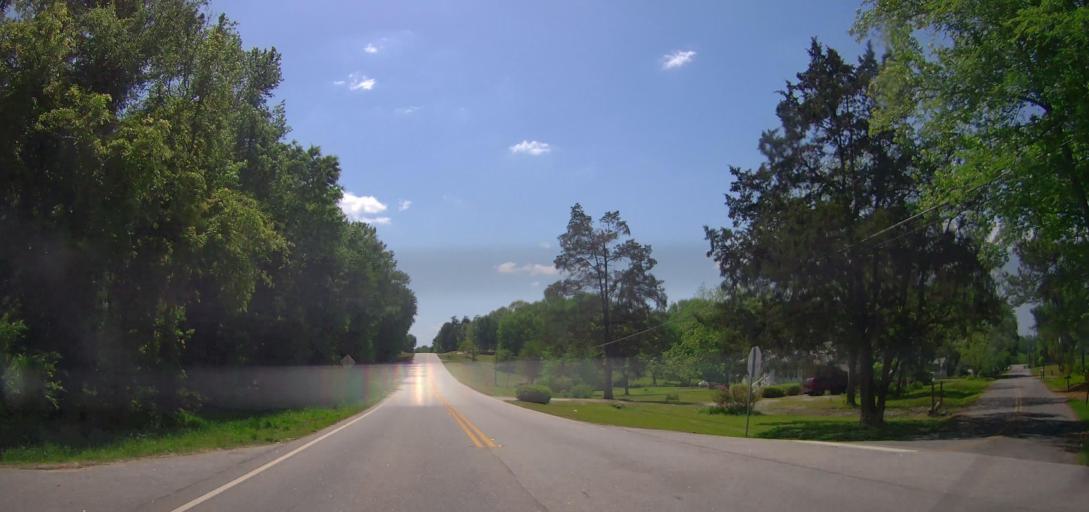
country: US
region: Georgia
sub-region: Putnam County
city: Eatonton
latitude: 33.3387
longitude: -83.3615
